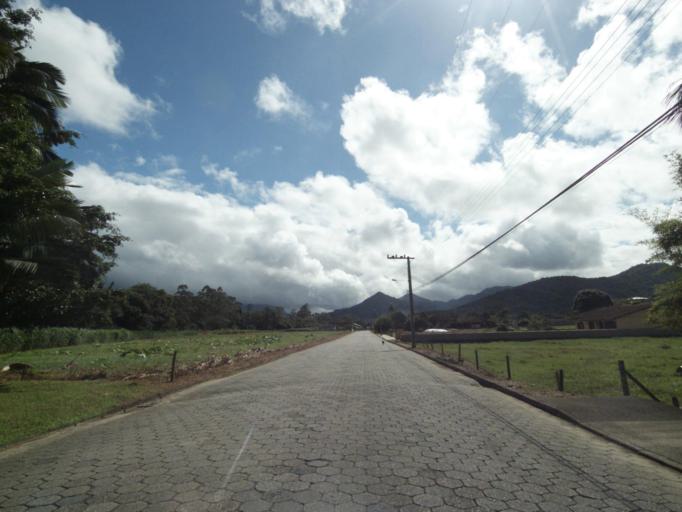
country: BR
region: Santa Catarina
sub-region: Pomerode
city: Pomerode
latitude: -26.6956
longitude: -49.1735
